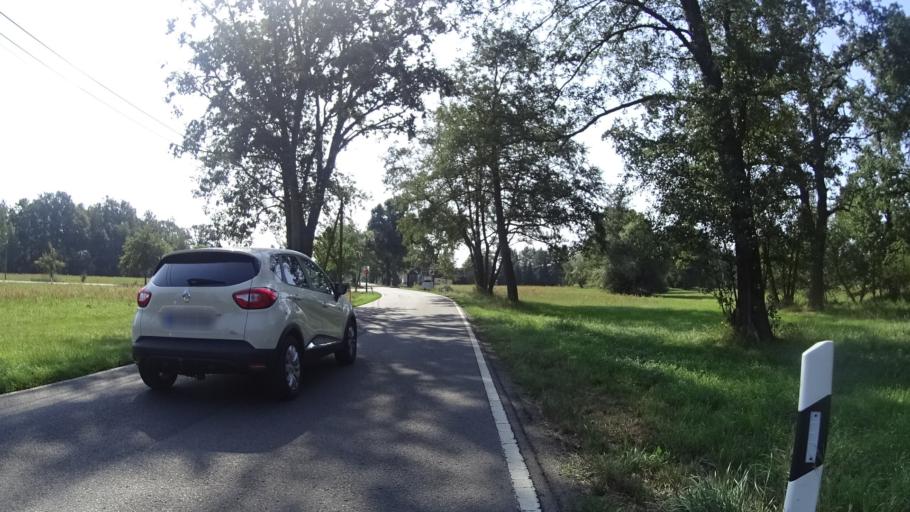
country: DE
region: Brandenburg
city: Burg
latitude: 51.8560
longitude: 14.1312
